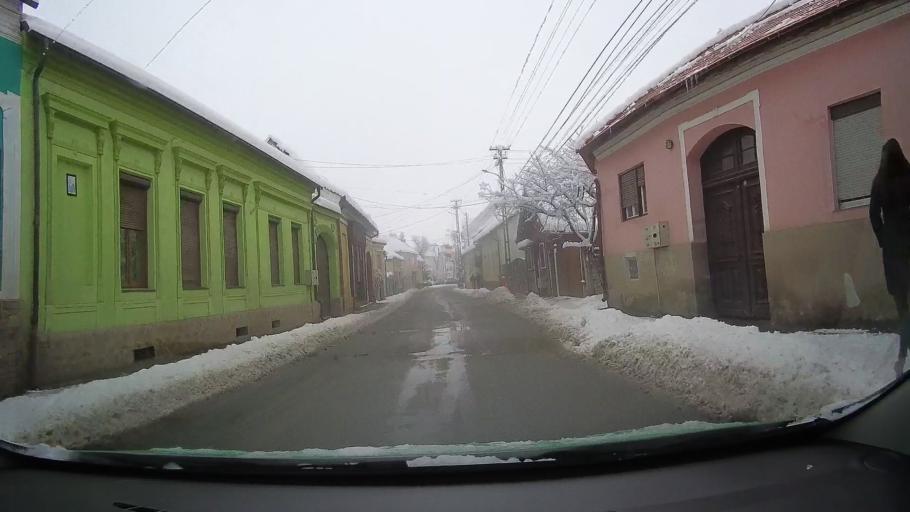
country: RO
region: Sibiu
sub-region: Oras Saliste
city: Saliste
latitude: 45.7939
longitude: 23.8824
